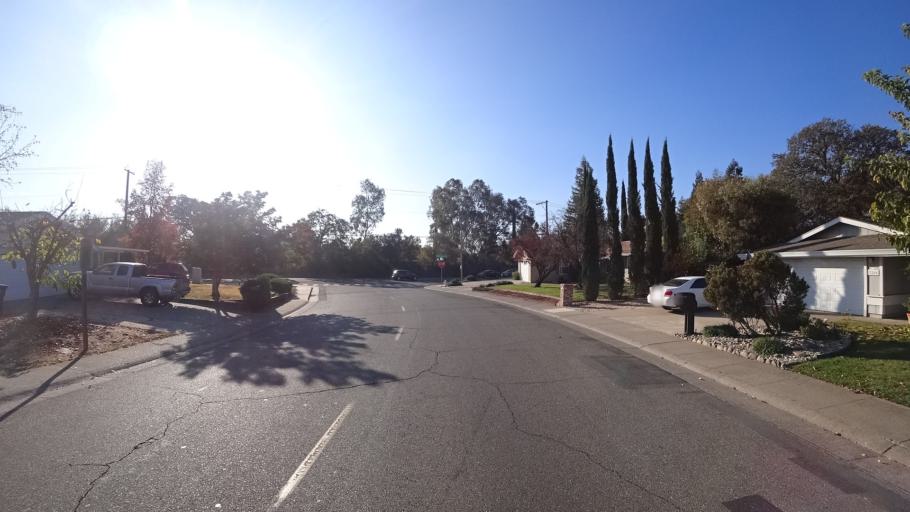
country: US
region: California
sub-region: Sacramento County
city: Citrus Heights
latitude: 38.7089
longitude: -121.2620
